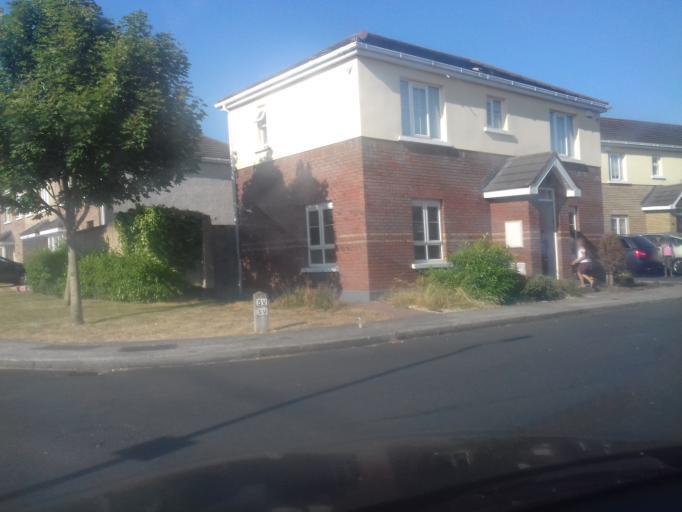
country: IE
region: Leinster
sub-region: Fingal County
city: Blanchardstown
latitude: 53.4213
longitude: -6.3954
